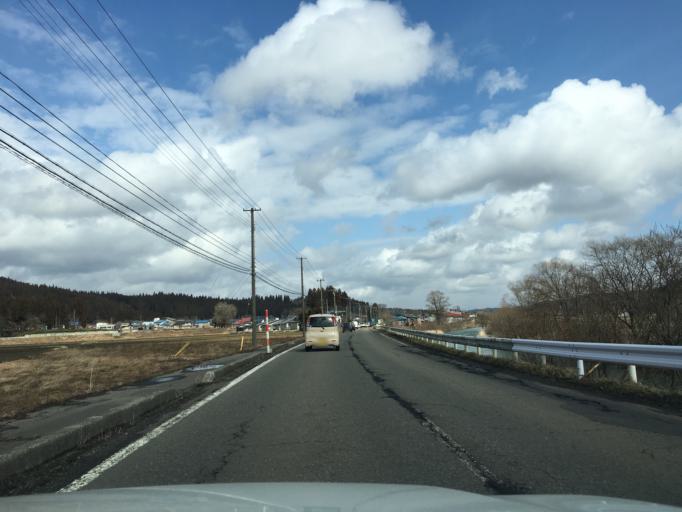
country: JP
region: Akita
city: Takanosu
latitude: 40.0400
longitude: 140.2794
